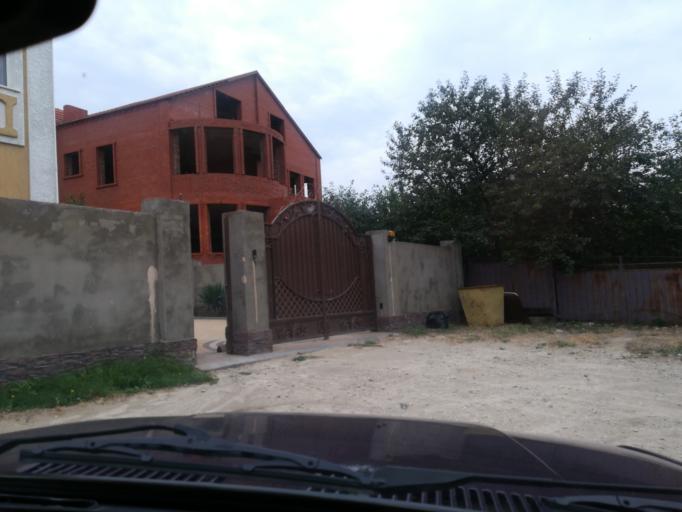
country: RU
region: Krasnodarskiy
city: Vityazevo
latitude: 45.0165
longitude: 37.2944
